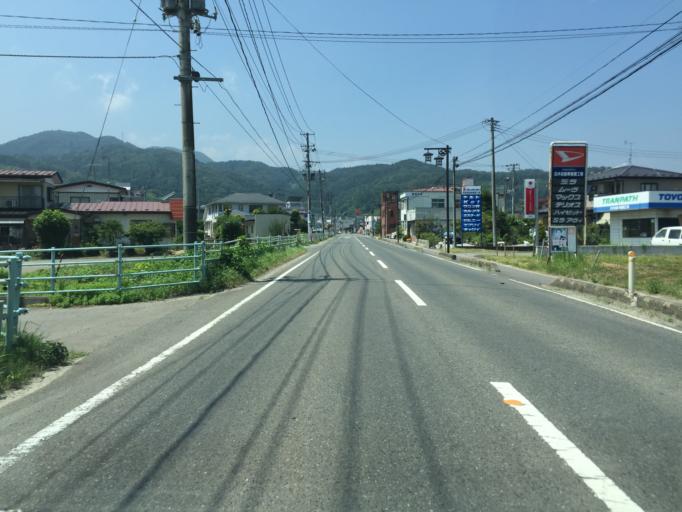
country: JP
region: Miyagi
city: Marumori
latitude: 37.9130
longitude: 140.7693
